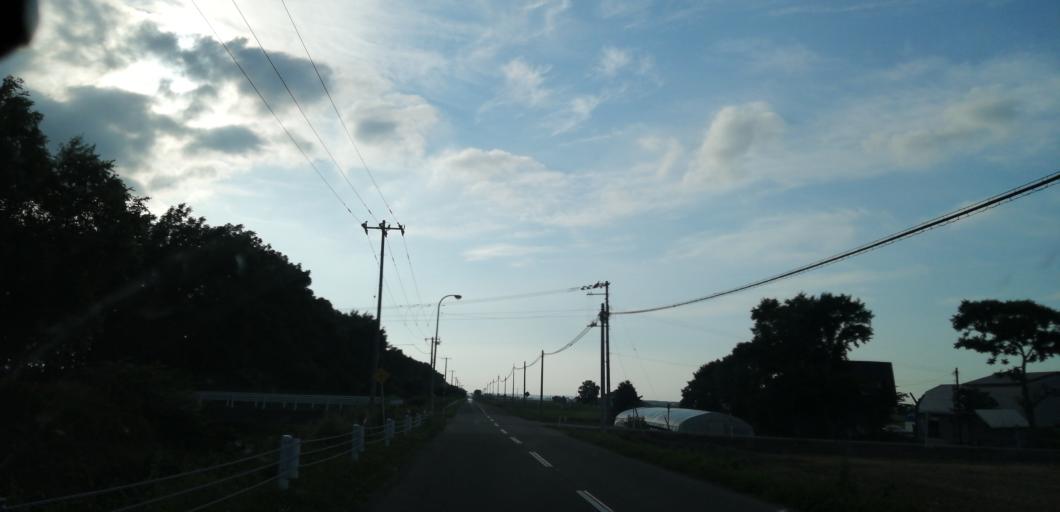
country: JP
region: Hokkaido
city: Chitose
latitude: 42.9396
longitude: 141.6996
